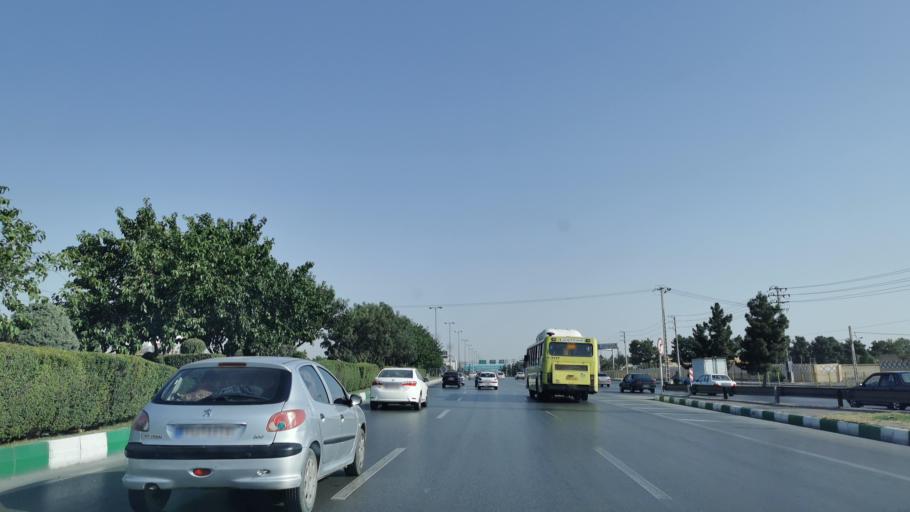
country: IR
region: Razavi Khorasan
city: Mashhad
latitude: 36.3482
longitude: 59.5470
